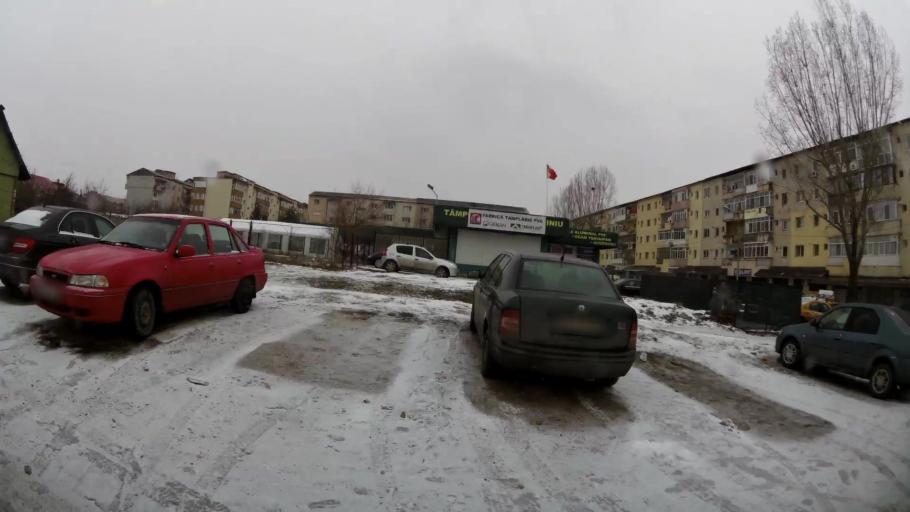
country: RO
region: Dambovita
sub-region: Municipiul Targoviste
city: Targoviste
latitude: 44.9334
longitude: 25.4447
